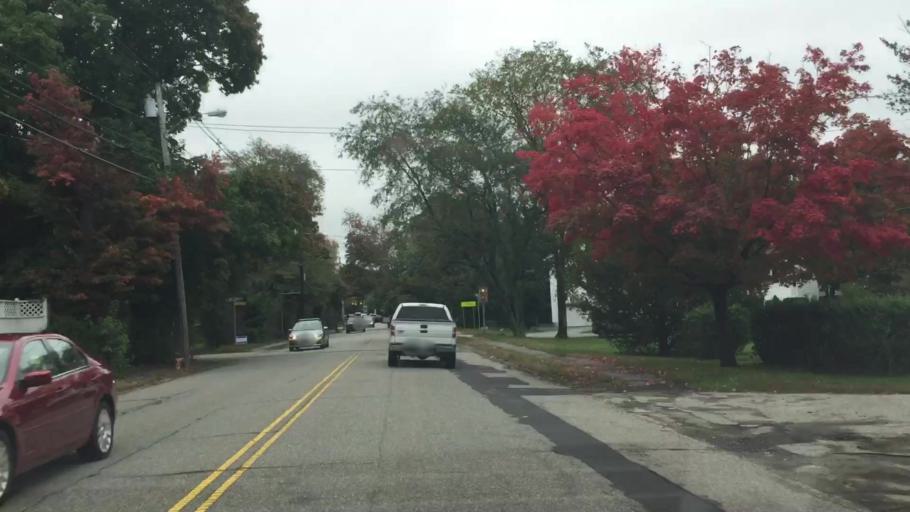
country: US
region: Massachusetts
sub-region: Essex County
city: North Andover
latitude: 42.6893
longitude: -71.1252
